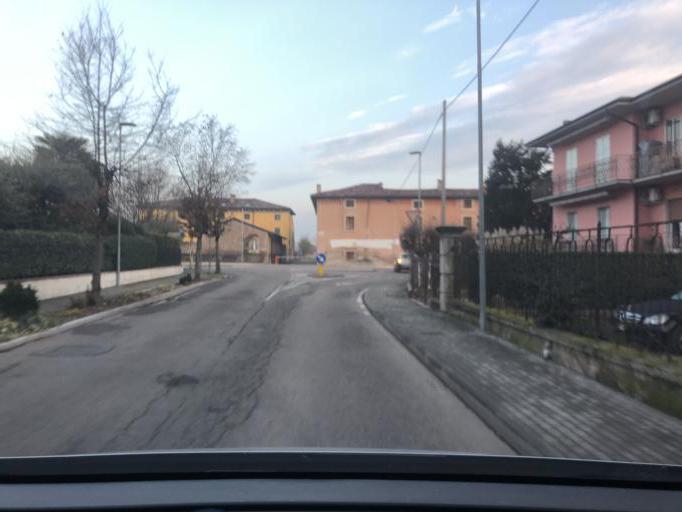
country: IT
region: Veneto
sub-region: Provincia di Verona
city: Caselle
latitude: 45.4166
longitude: 10.9048
